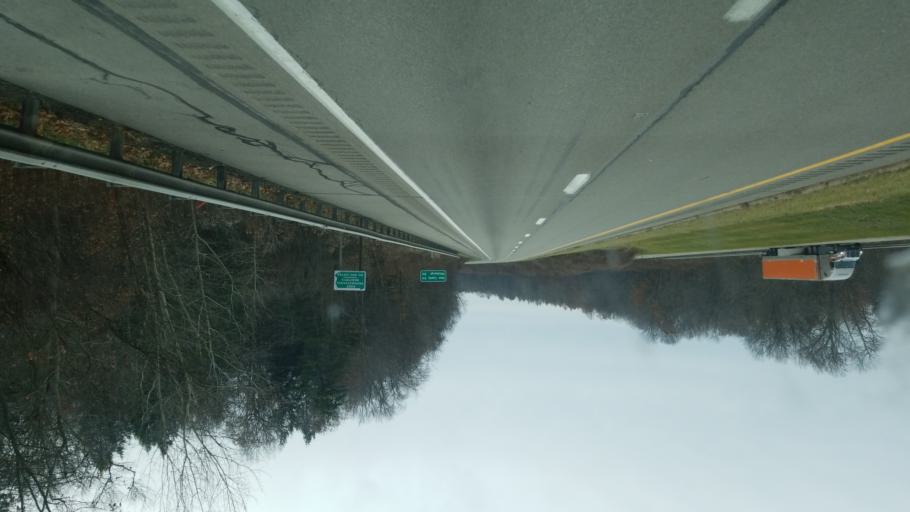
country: US
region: Pennsylvania
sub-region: Crawford County
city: Meadville
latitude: 41.5298
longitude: -80.1742
